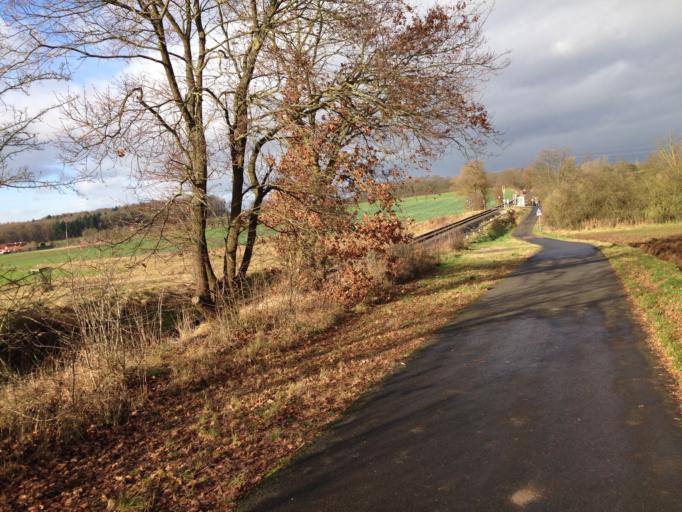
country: DE
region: Hesse
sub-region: Regierungsbezirk Giessen
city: Hungen
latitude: 50.4608
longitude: 8.9053
